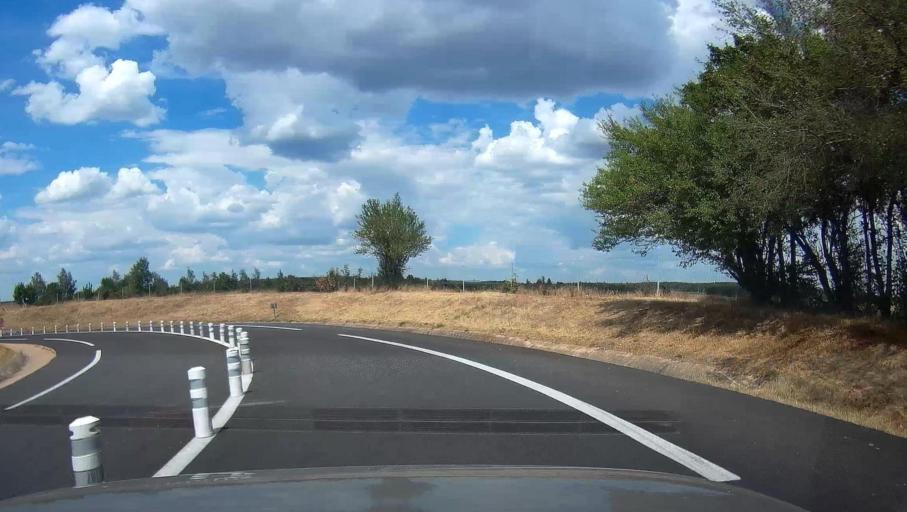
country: FR
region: Bourgogne
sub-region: Departement de la Cote-d'Or
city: Selongey
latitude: 47.5410
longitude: 5.2006
